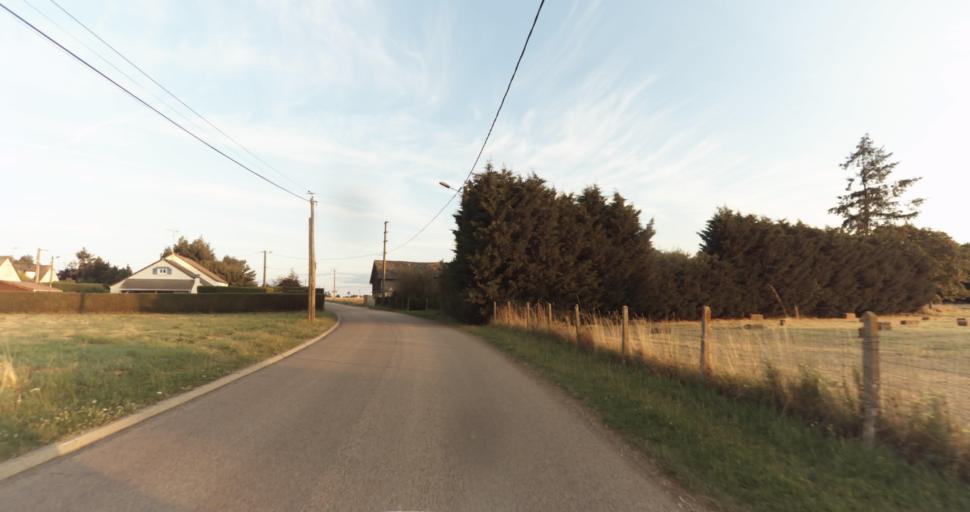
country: FR
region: Haute-Normandie
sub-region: Departement de l'Eure
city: La Madeleine-de-Nonancourt
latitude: 48.8866
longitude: 1.1955
